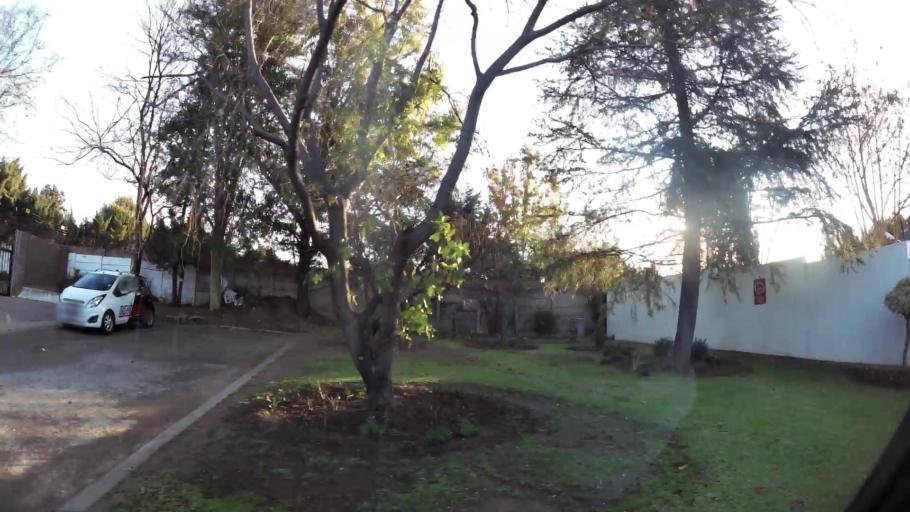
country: ZA
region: Gauteng
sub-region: City of Johannesburg Metropolitan Municipality
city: Diepsloot
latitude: -26.0373
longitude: 27.9811
